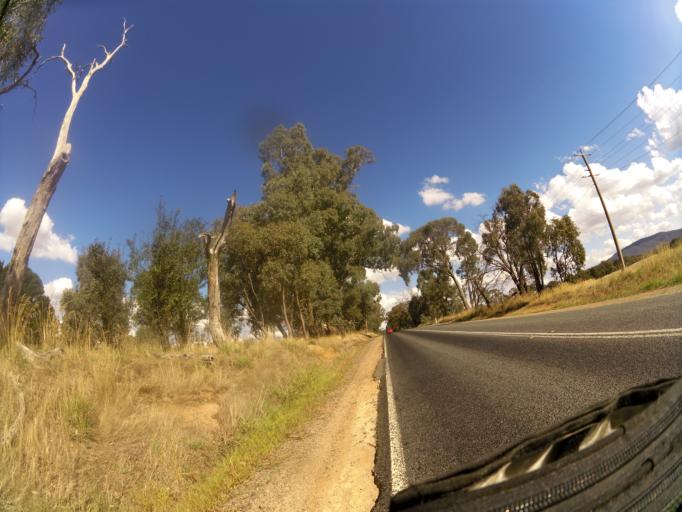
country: AU
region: Victoria
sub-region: Mansfield
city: Mansfield
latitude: -36.9132
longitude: 146.0004
